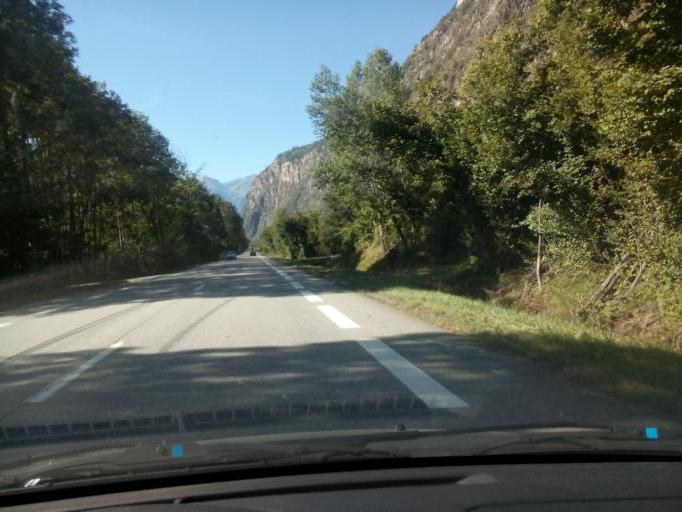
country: FR
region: Rhone-Alpes
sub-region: Departement de l'Isere
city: Huez
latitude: 45.0348
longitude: 6.0659
